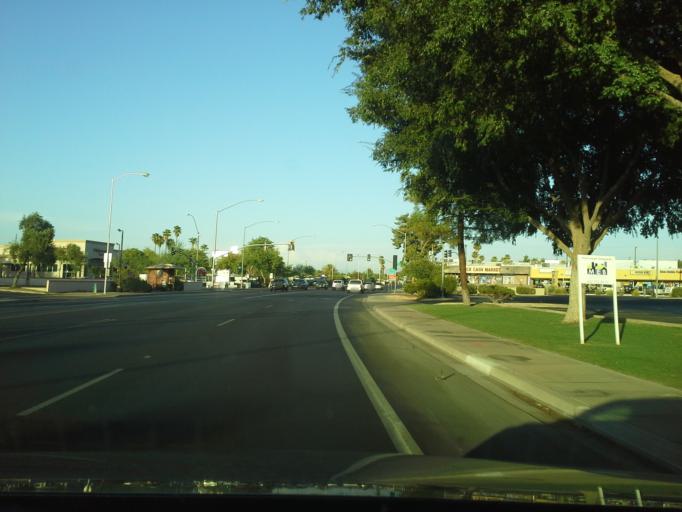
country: US
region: Arizona
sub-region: Maricopa County
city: Mesa
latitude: 33.4354
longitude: -111.8239
